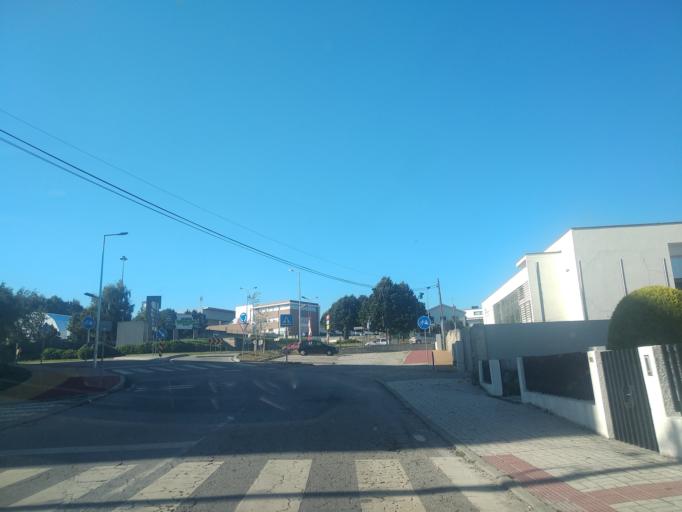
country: PT
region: Porto
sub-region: Penafiel
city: Penafiel
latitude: 41.2025
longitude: -8.2719
